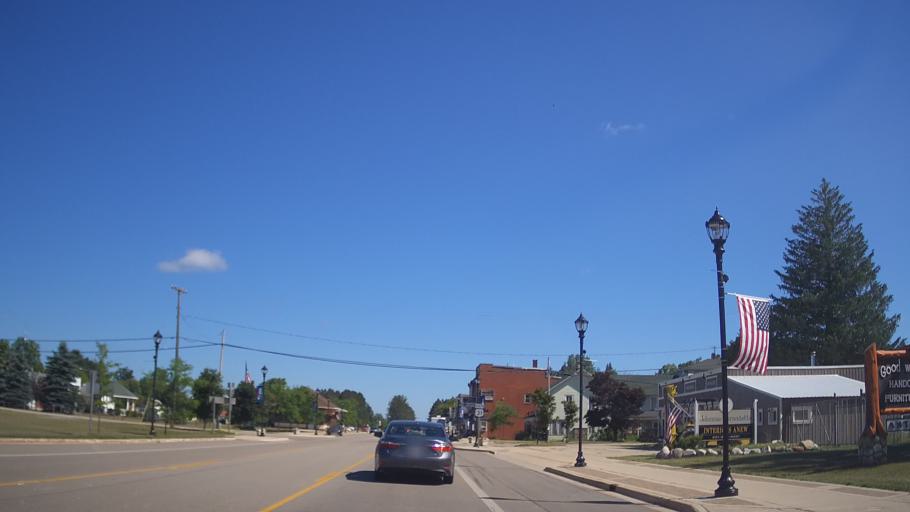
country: US
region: Michigan
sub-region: Cheboygan County
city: Indian River
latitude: 45.5515
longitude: -84.7844
